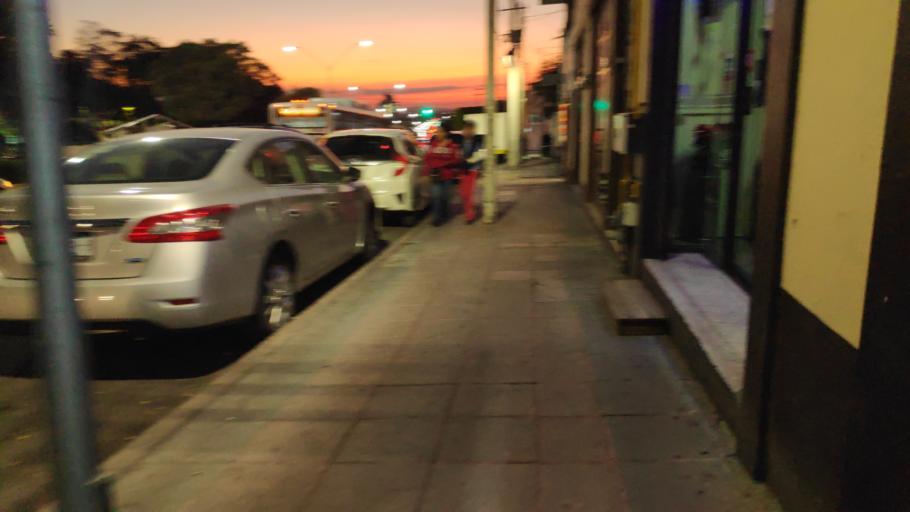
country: MX
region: Queretaro
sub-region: Queretaro
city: Santiago de Queretaro
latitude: 20.5914
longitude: -100.3830
